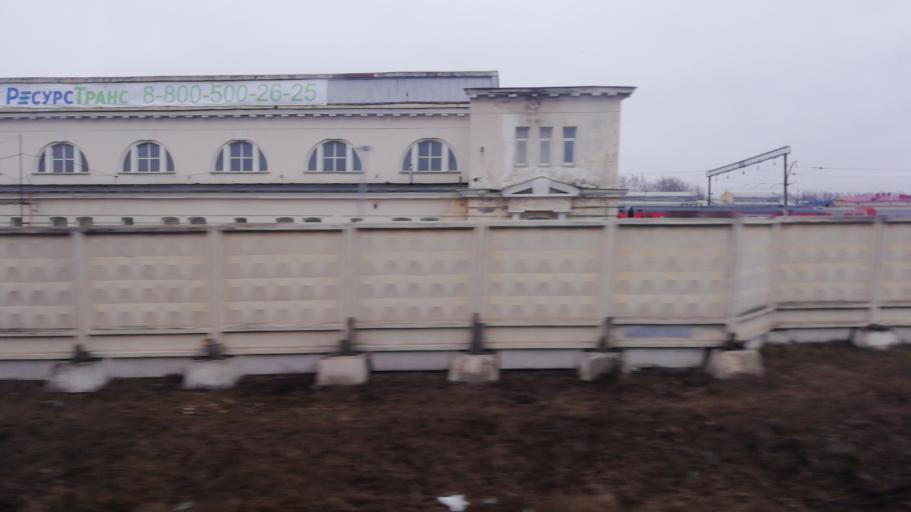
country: RU
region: St.-Petersburg
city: Kupchino
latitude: 59.8860
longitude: 30.3454
